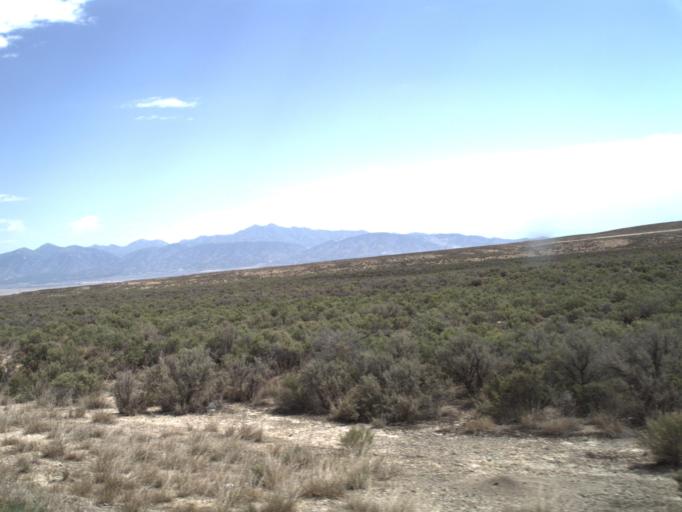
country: US
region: Utah
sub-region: Tooele County
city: Tooele
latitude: 40.1488
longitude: -112.4307
